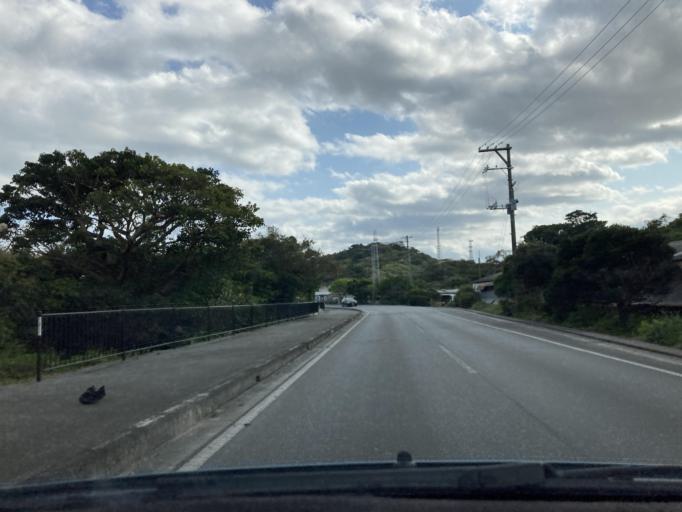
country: JP
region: Okinawa
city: Tomigusuku
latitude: 26.1782
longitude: 127.7608
